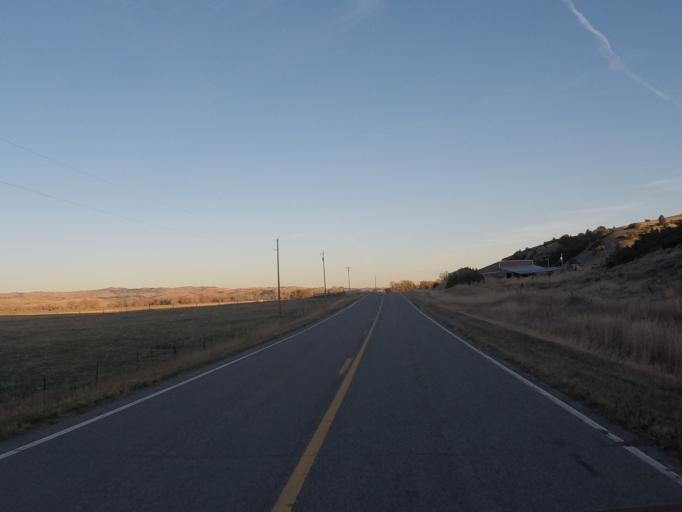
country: US
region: Montana
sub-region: Sweet Grass County
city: Big Timber
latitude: 45.7803
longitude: -109.8193
